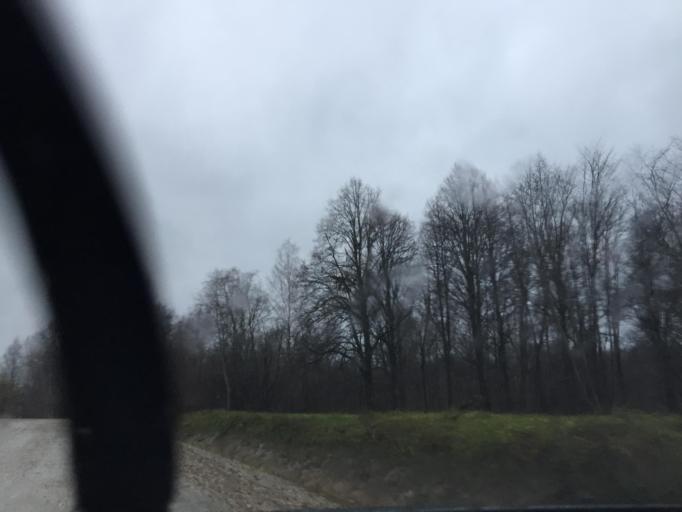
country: LV
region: Salacgrivas
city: Salacgriva
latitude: 57.7615
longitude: 24.4561
